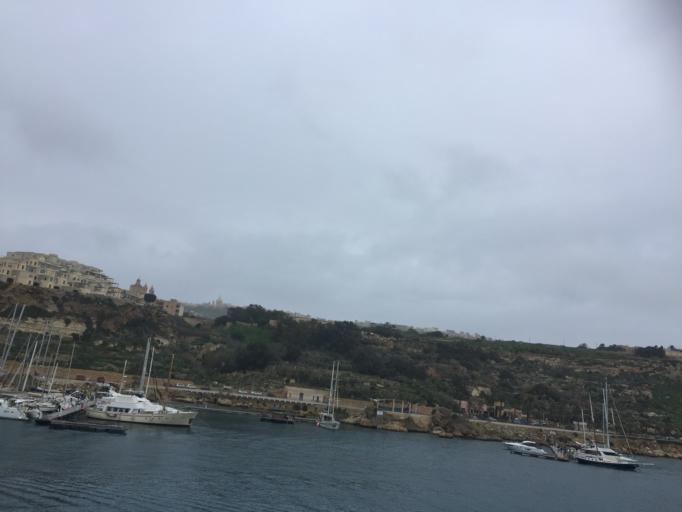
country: MT
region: Ghajnsielem
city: Mgarr
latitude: 36.0249
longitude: 14.2994
